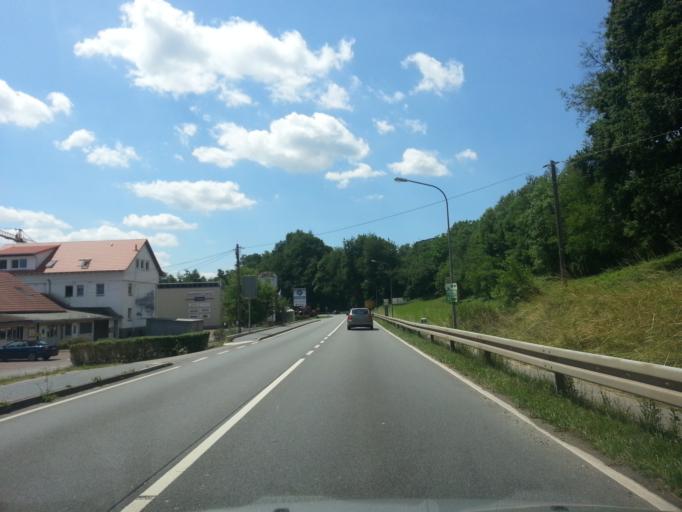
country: DE
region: Hesse
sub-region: Regierungsbezirk Darmstadt
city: Morlenbach
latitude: 49.5922
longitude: 8.7299
